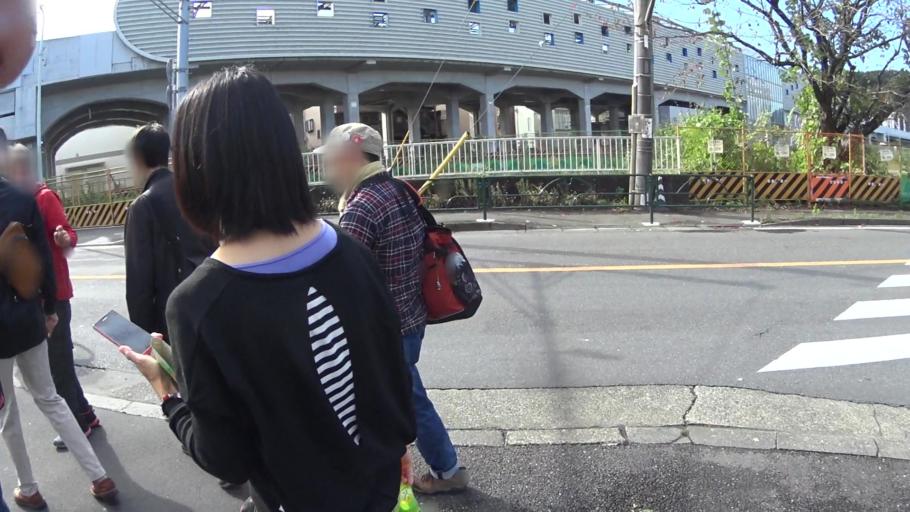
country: JP
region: Tokyo
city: Kokubunji
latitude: 35.6488
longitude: 139.4903
